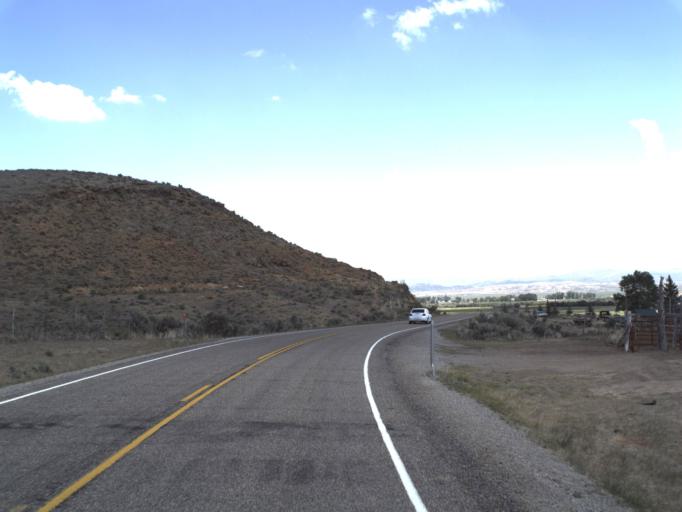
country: US
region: Utah
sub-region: Rich County
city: Randolph
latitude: 41.5195
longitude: -111.2013
